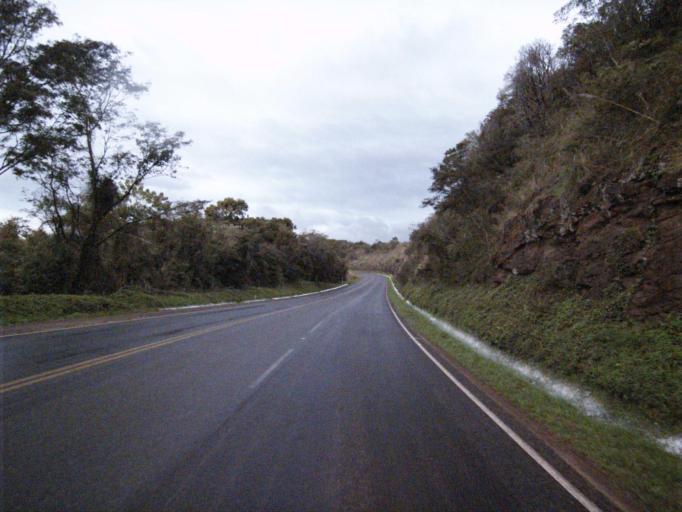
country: BR
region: Santa Catarina
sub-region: Concordia
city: Concordia
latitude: -27.0543
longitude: -51.8887
